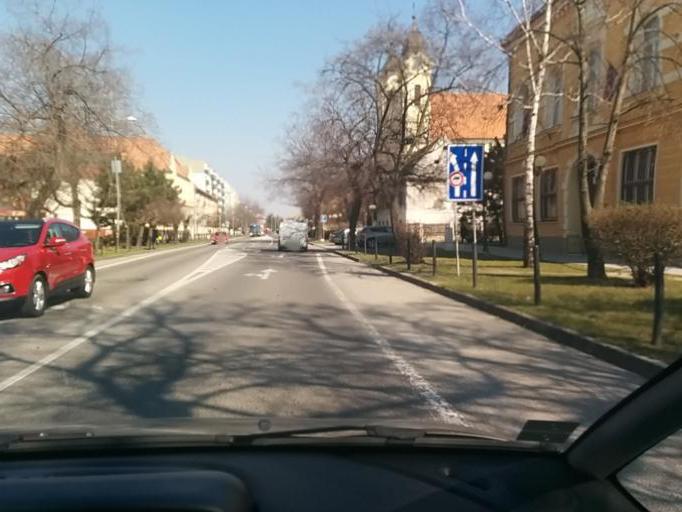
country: SK
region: Trnavsky
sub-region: Okres Galanta
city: Galanta
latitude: 48.1913
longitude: 17.7311
